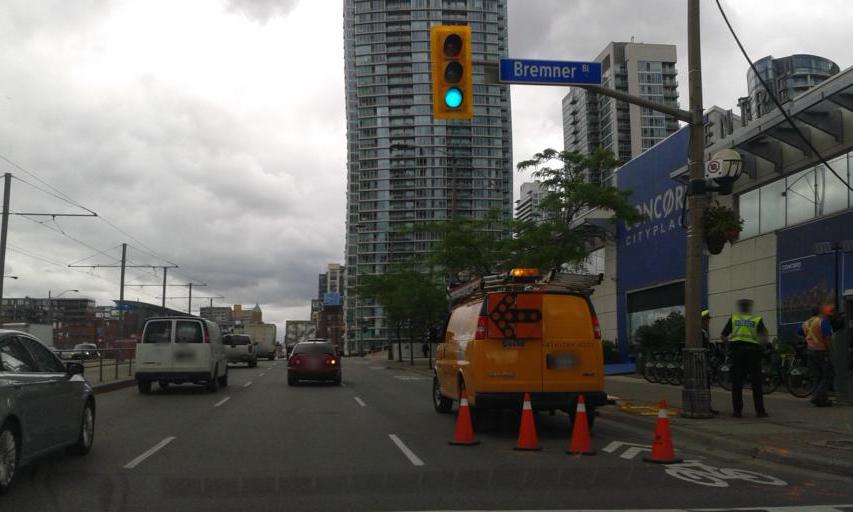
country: CA
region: Ontario
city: Toronto
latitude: 43.6404
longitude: -79.3928
